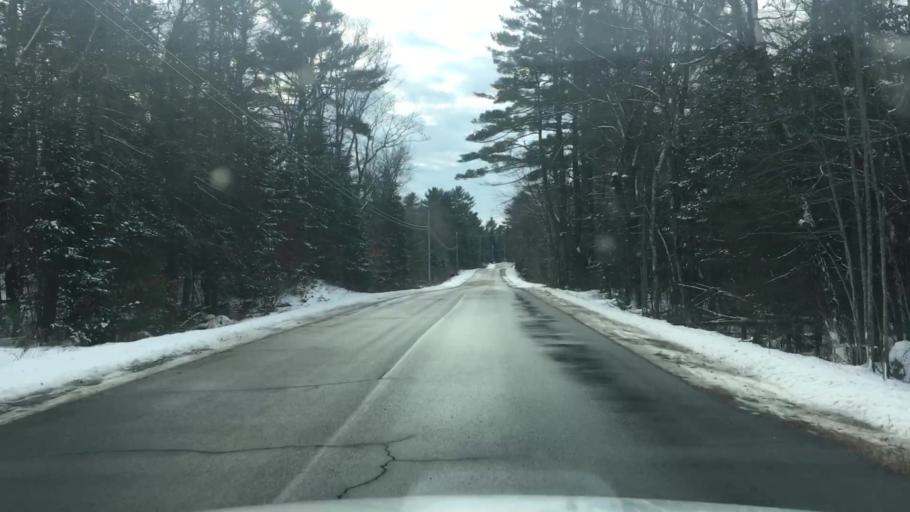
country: US
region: Maine
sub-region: Kennebec County
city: Chelsea
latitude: 44.2838
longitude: -69.6674
